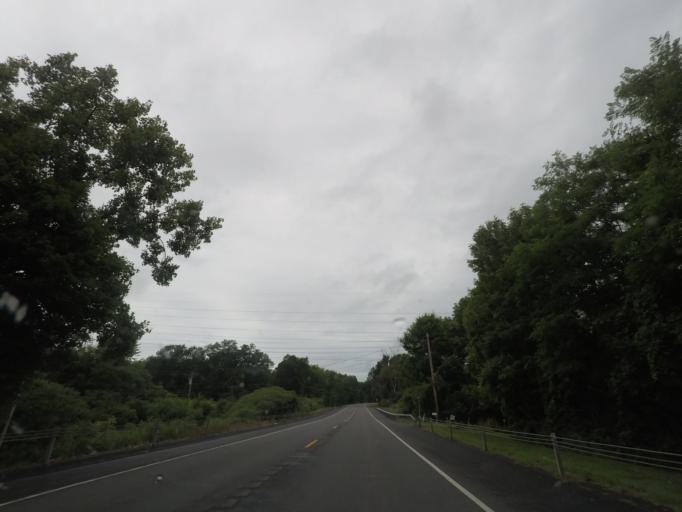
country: US
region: New York
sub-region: Rensselaer County
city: Hampton Manor
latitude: 42.6204
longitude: -73.7108
